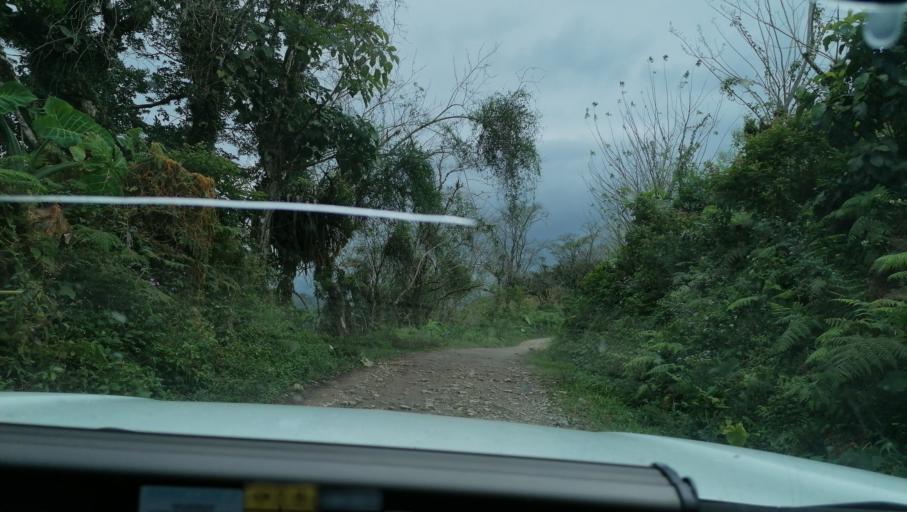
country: MX
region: Chiapas
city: Ixtacomitan
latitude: 17.3475
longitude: -93.1410
